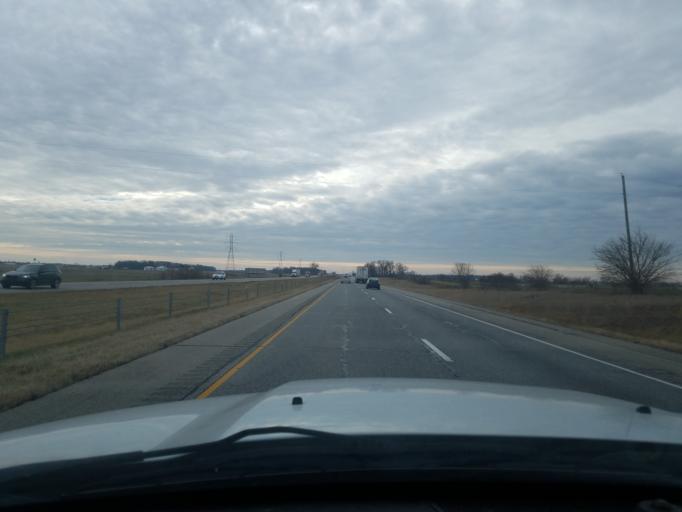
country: US
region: Indiana
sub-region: Huntington County
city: Warren
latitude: 40.6483
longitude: -85.5083
